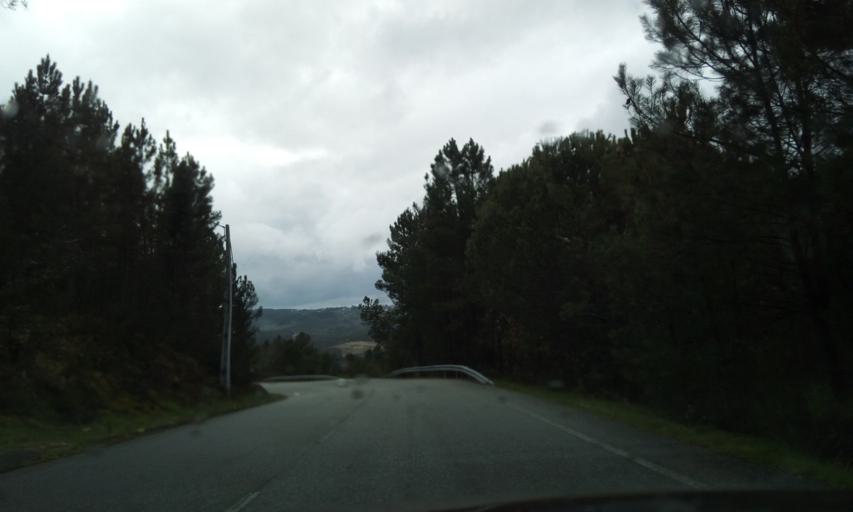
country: PT
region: Viseu
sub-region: Viseu
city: Rio de Loba
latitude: 40.6048
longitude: -7.8480
